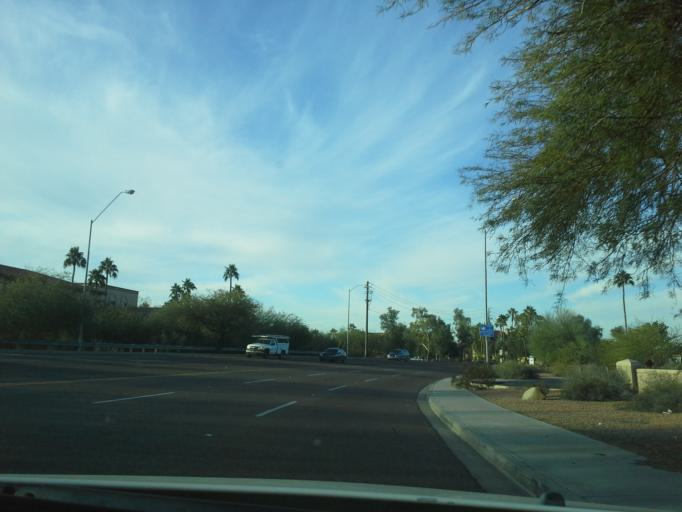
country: US
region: Arizona
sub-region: Maricopa County
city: Phoenix
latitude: 33.5538
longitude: -112.0492
